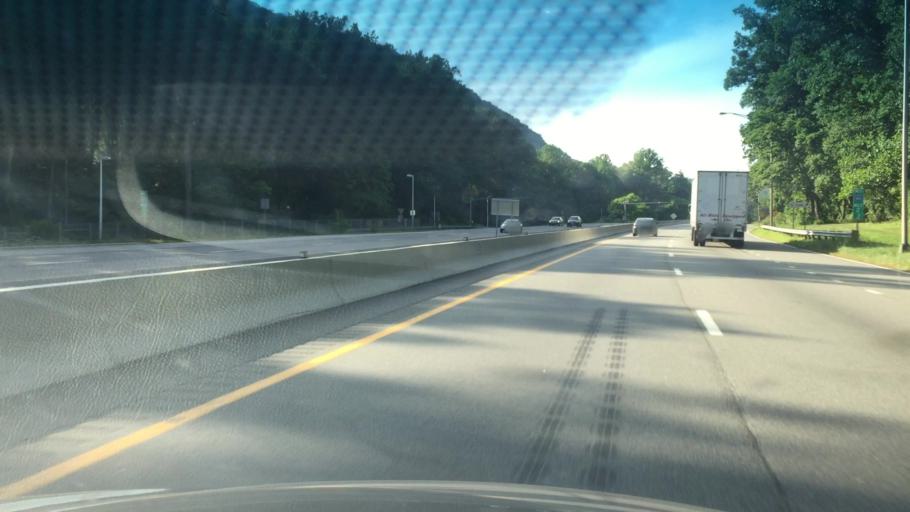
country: US
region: Pennsylvania
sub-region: Monroe County
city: East Stroudsburg
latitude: 40.9545
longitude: -75.1156
